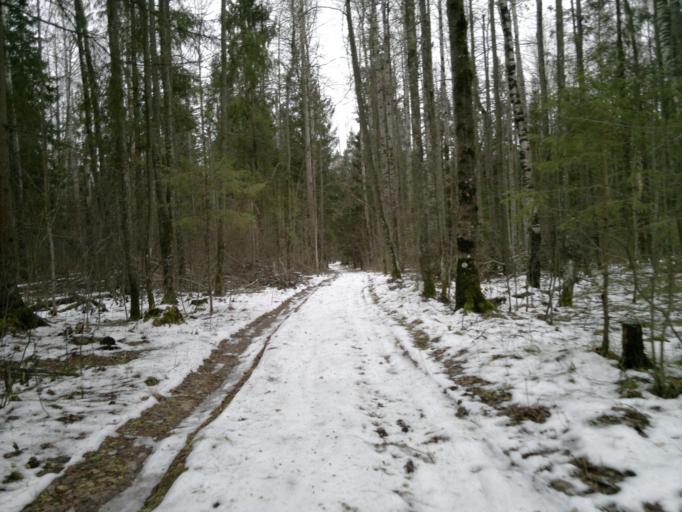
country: RU
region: Mariy-El
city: Yoshkar-Ola
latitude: 56.6046
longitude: 47.9623
